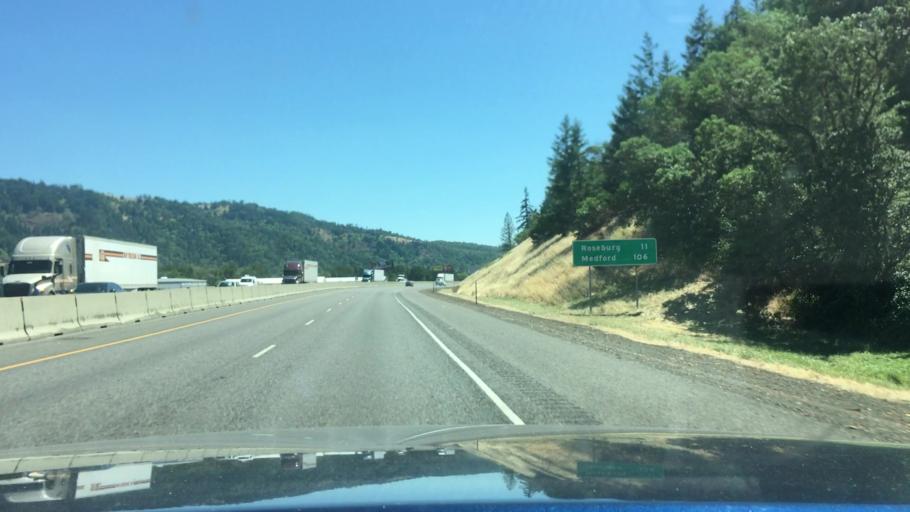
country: US
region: Oregon
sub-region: Douglas County
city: Sutherlin
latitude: 43.3575
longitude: -123.3276
